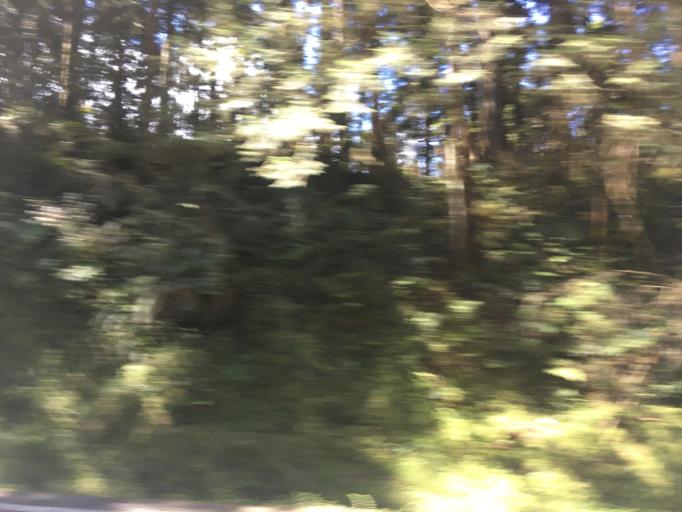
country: TW
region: Taiwan
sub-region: Yilan
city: Yilan
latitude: 24.5220
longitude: 121.5154
